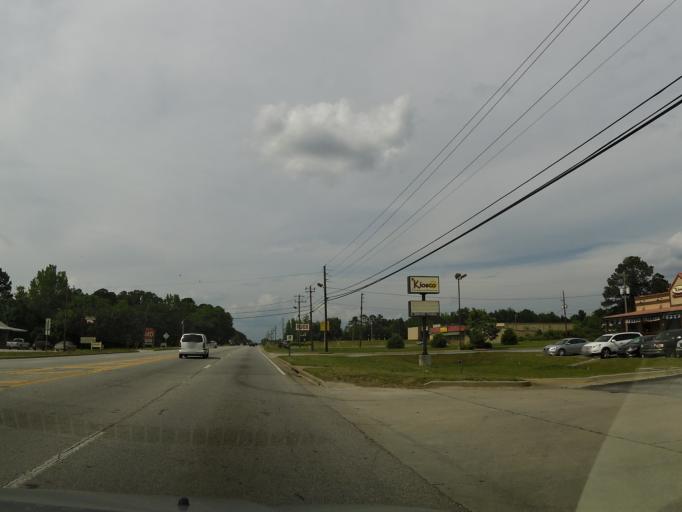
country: US
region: Georgia
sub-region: McDuffie County
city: Thomson
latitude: 33.4850
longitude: -82.5051
